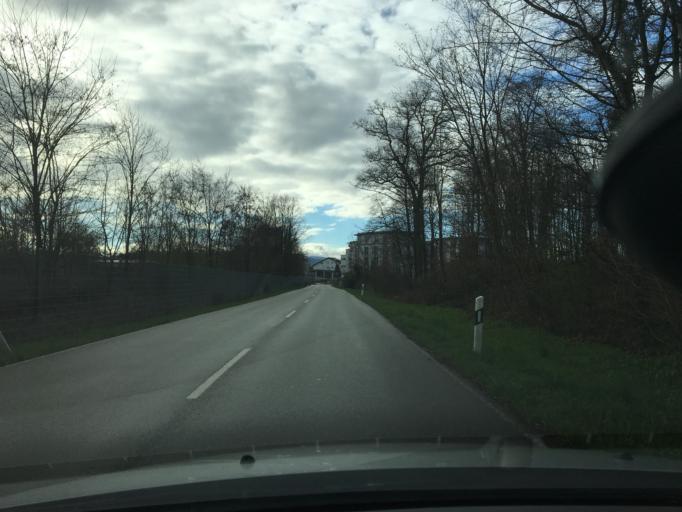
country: DE
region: Baden-Wuerttemberg
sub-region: Freiburg Region
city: Umkirch
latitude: 48.0399
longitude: 7.7597
